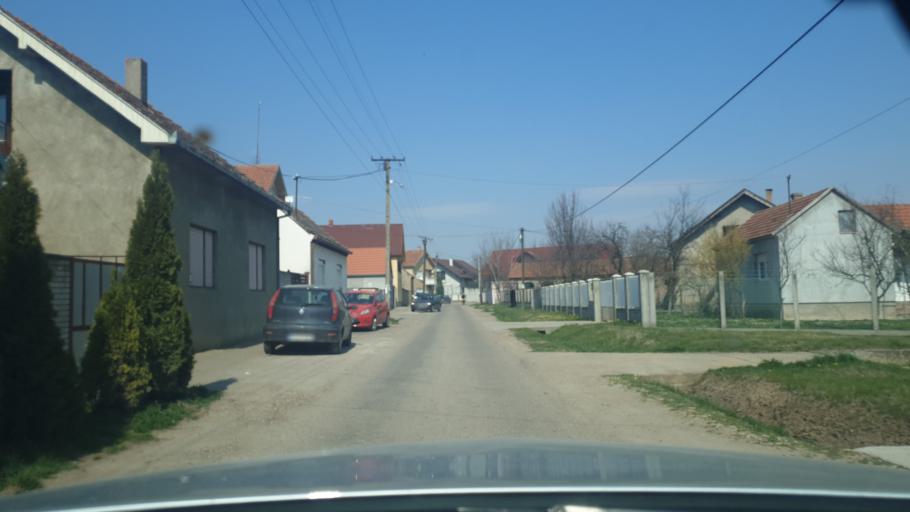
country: RS
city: Putinci
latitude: 44.9929
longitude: 19.9635
